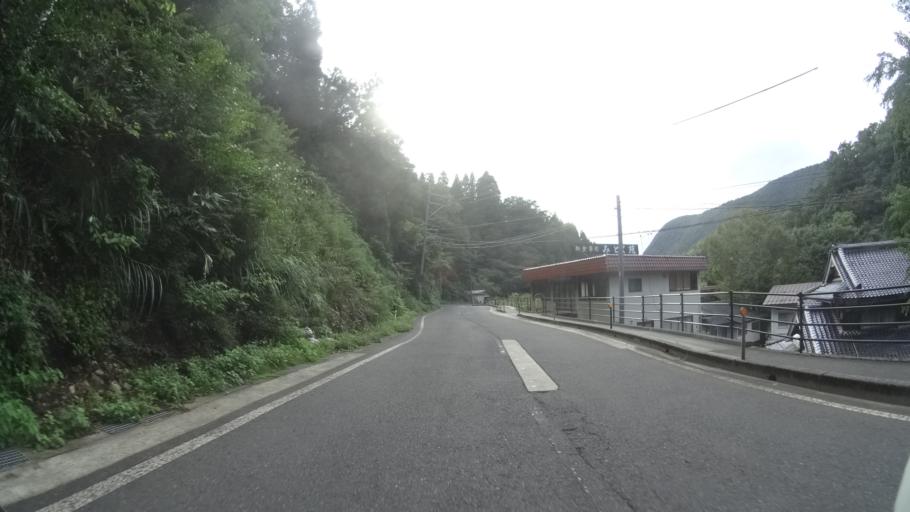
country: JP
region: Tottori
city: Kurayoshi
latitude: 35.4003
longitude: 133.9587
